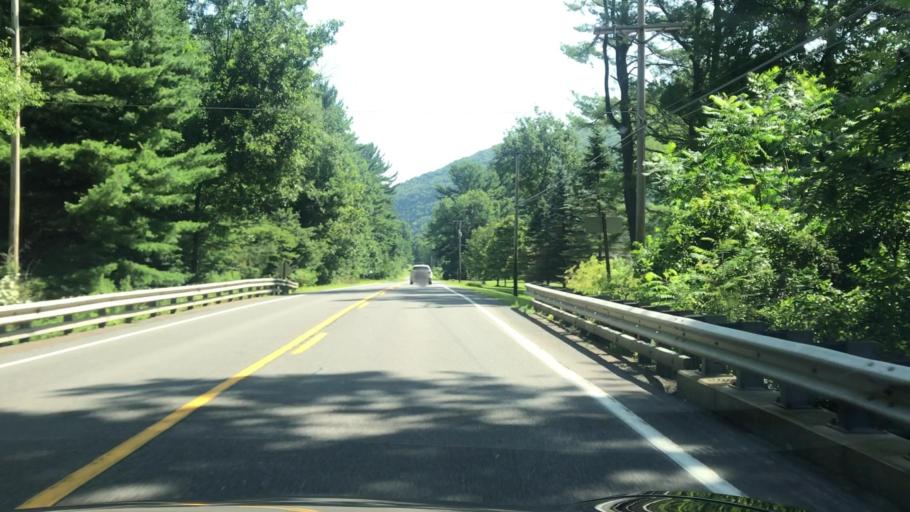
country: US
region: Pennsylvania
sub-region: Bradford County
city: Canton
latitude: 41.4867
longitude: -76.9734
